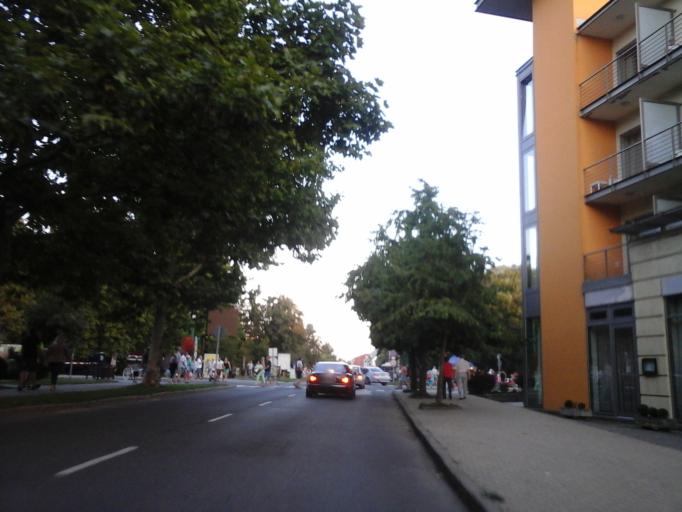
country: HU
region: Hajdu-Bihar
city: Hajduszoboszlo
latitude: 47.4512
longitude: 21.4016
